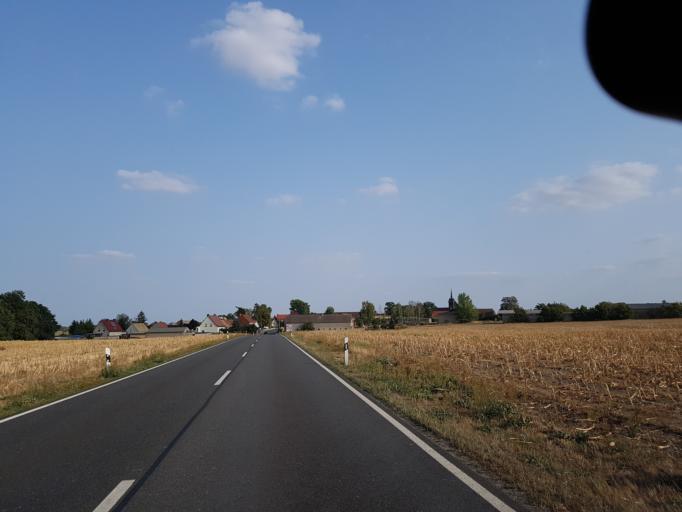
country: DE
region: Saxony
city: Dommitzsch
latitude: 51.6646
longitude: 12.8473
